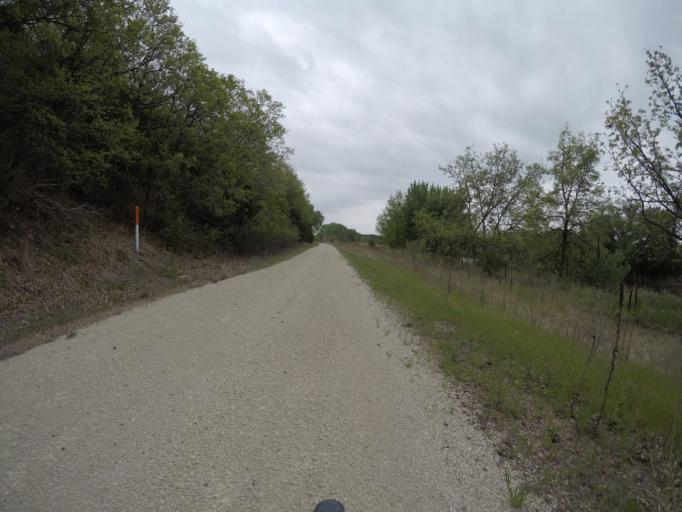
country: US
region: Nebraska
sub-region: Gage County
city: Wymore
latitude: 40.1122
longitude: -96.6247
